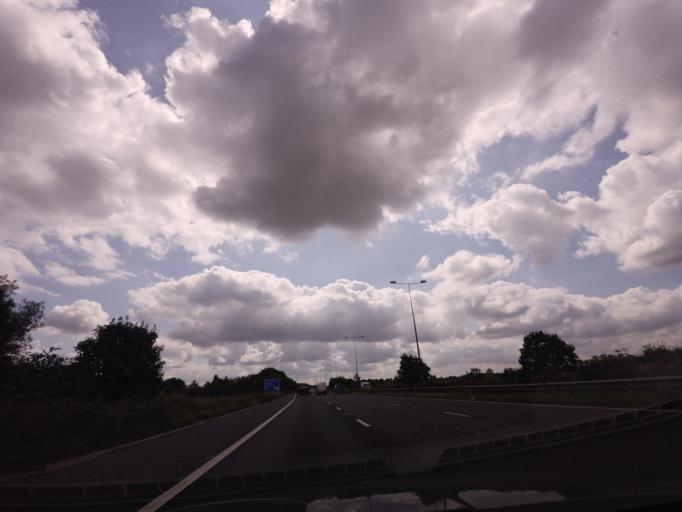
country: GB
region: England
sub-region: Borough of Wigan
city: Shevington
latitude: 53.5509
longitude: -2.7008
